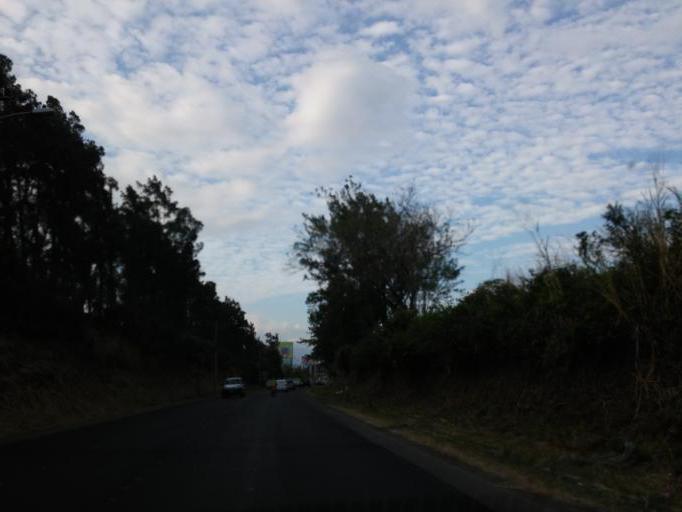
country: CR
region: Heredia
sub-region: Canton de Belen
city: San Antonio
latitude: 9.9694
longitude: -84.2001
